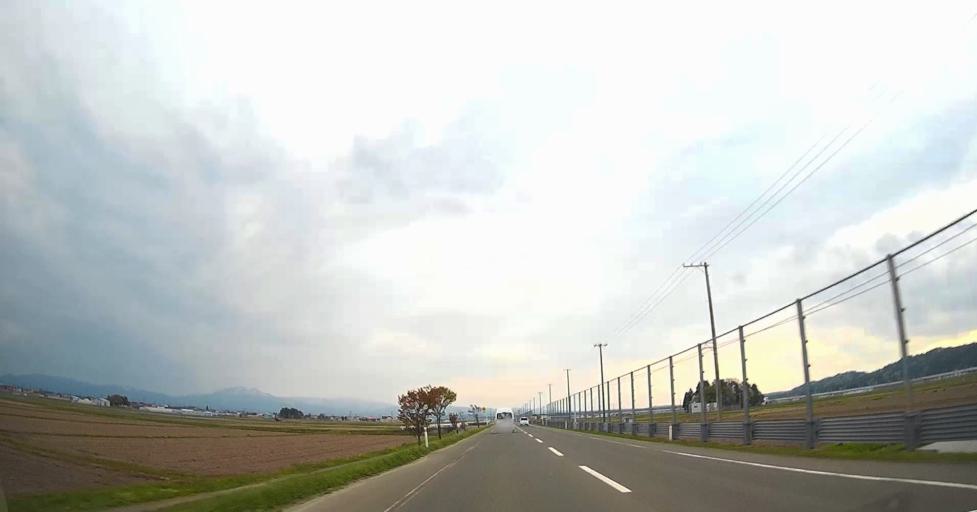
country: JP
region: Aomori
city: Aomori Shi
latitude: 40.8956
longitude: 140.6682
